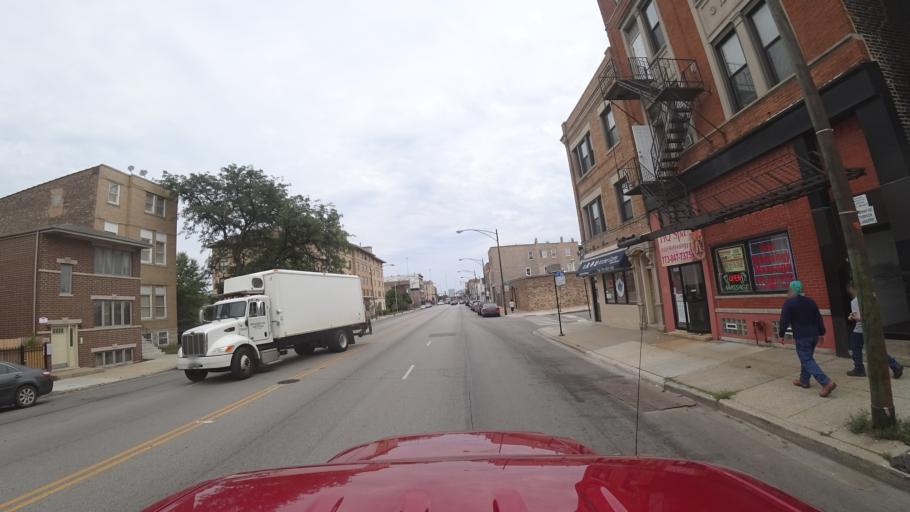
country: US
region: Illinois
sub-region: Cook County
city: Chicago
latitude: 41.8407
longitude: -87.6597
